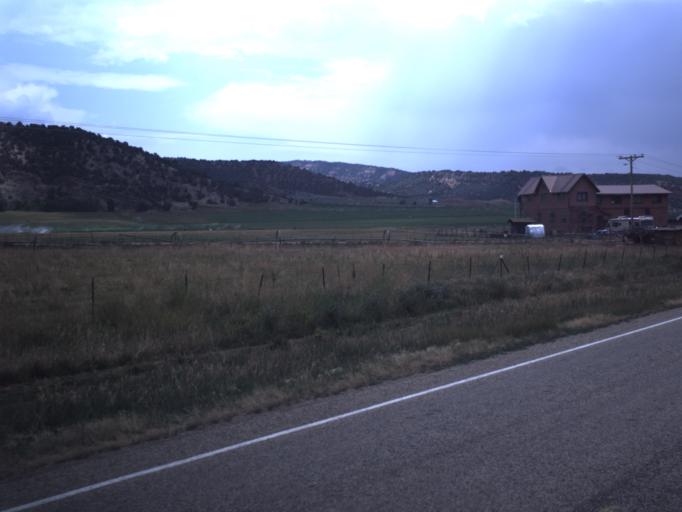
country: US
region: Utah
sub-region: Duchesne County
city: Duchesne
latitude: 40.4360
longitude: -110.8095
